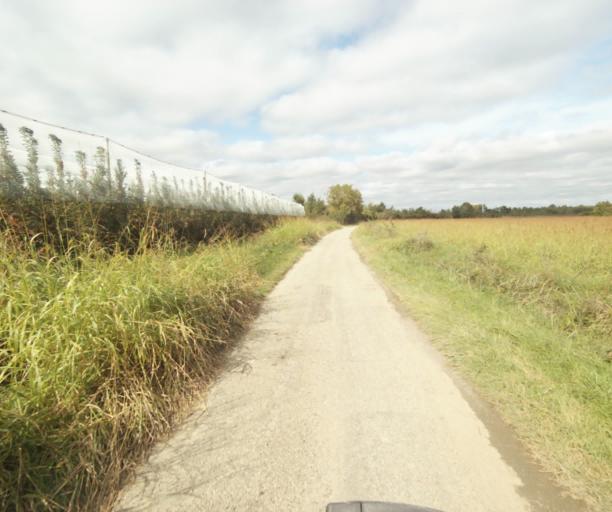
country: FR
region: Midi-Pyrenees
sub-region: Departement du Tarn-et-Garonne
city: Finhan
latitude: 43.9202
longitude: 1.2084
